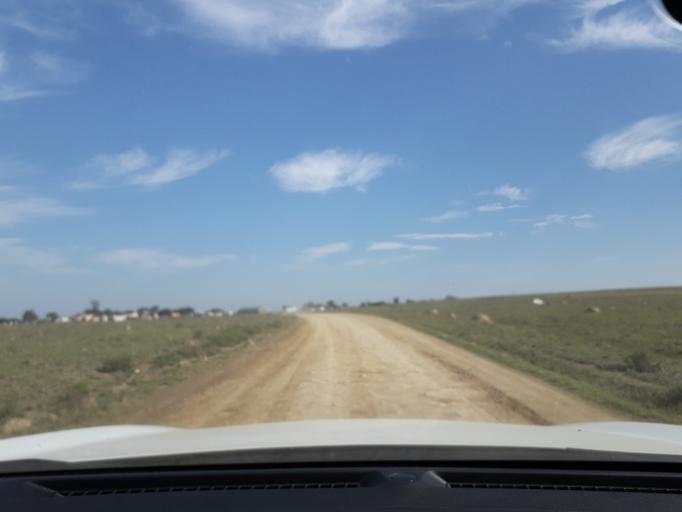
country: ZA
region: Eastern Cape
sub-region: Buffalo City Metropolitan Municipality
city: Bhisho
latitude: -33.0057
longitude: 27.3118
